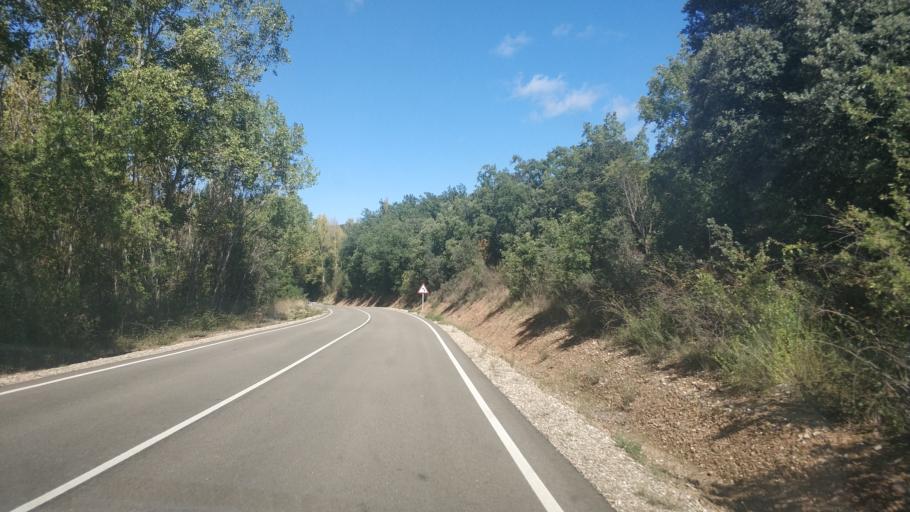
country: ES
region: Castille and Leon
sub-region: Provincia de Burgos
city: Covarrubias
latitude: 42.0491
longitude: -3.5502
